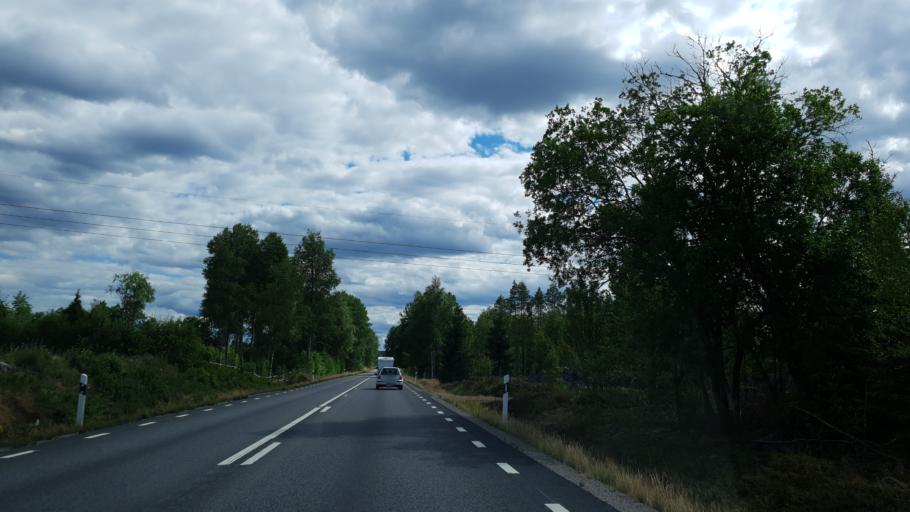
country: SE
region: Kronoberg
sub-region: Lessebo Kommun
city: Lessebo
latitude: 56.7971
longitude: 15.4121
